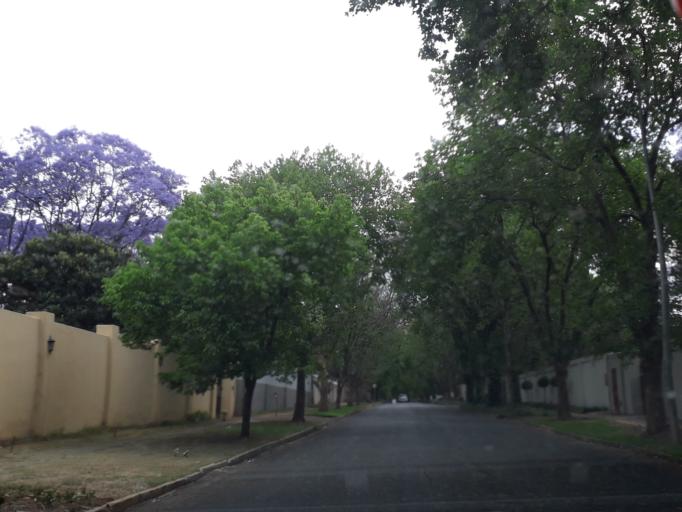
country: ZA
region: Gauteng
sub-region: City of Johannesburg Metropolitan Municipality
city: Johannesburg
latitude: -26.1559
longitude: 28.0445
